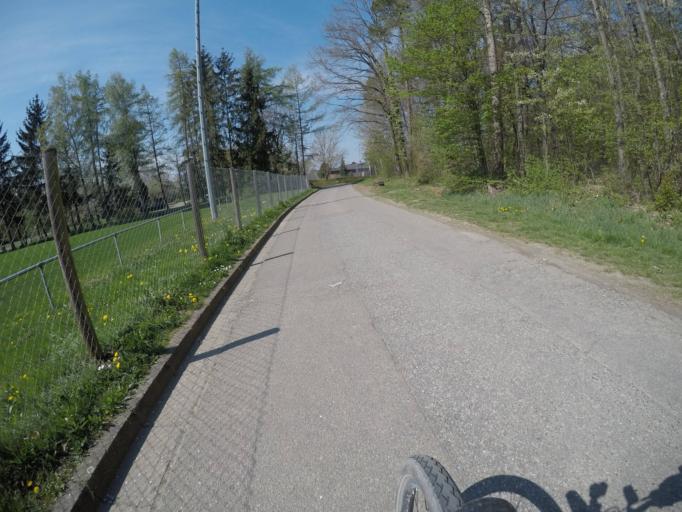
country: DE
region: Baden-Wuerttemberg
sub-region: Regierungsbezirk Stuttgart
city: Rutesheim
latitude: 48.8185
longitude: 8.9737
